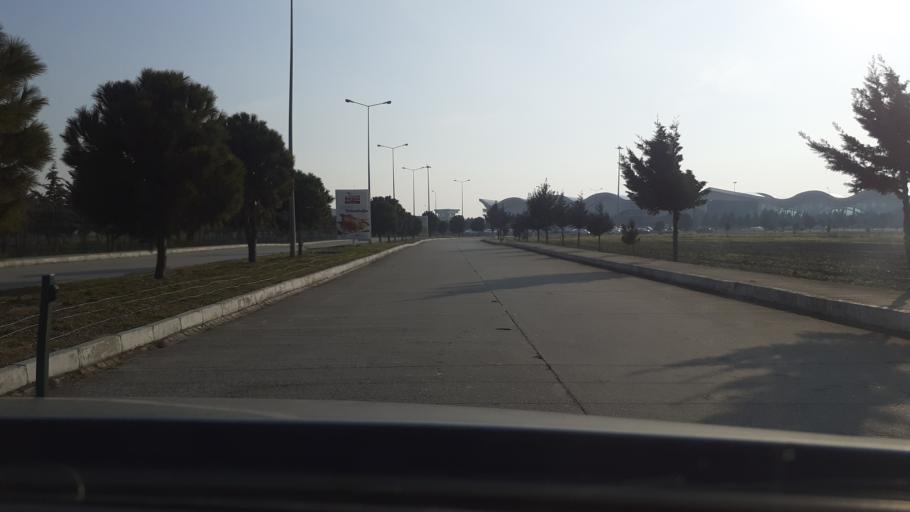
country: TR
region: Hatay
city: Serinyol
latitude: 36.3645
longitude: 36.2778
